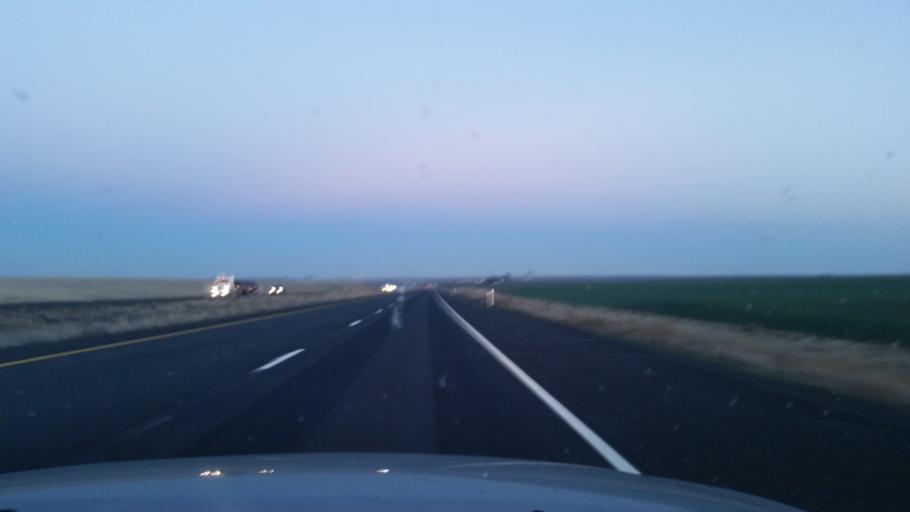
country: US
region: Washington
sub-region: Adams County
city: Ritzville
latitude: 47.1111
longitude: -118.4484
